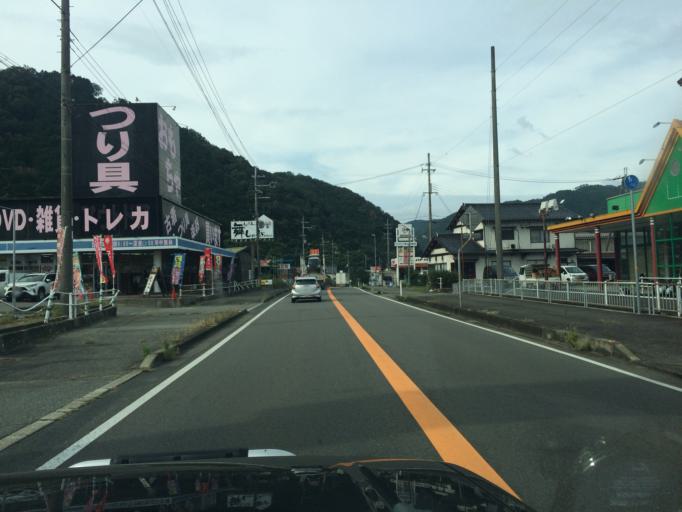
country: JP
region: Hyogo
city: Toyooka
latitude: 35.3481
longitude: 134.8371
